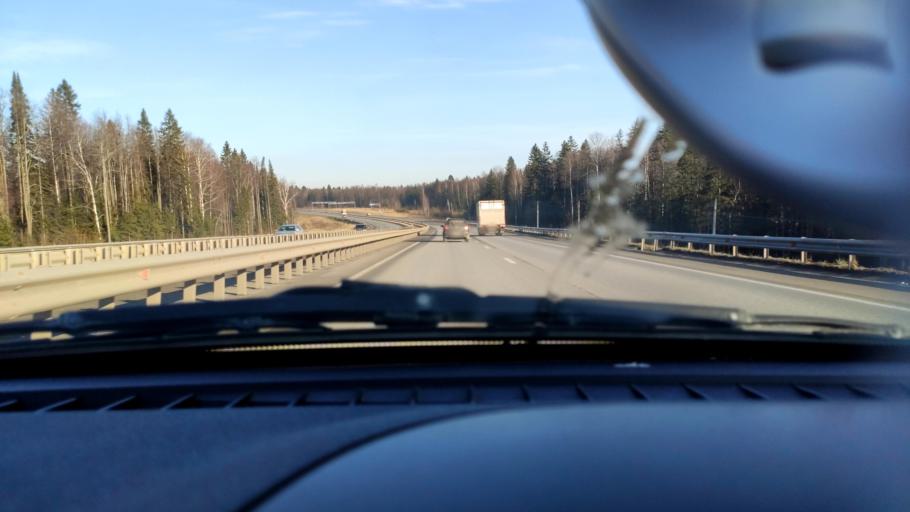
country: RU
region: Perm
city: Ferma
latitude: 58.0276
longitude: 56.4298
